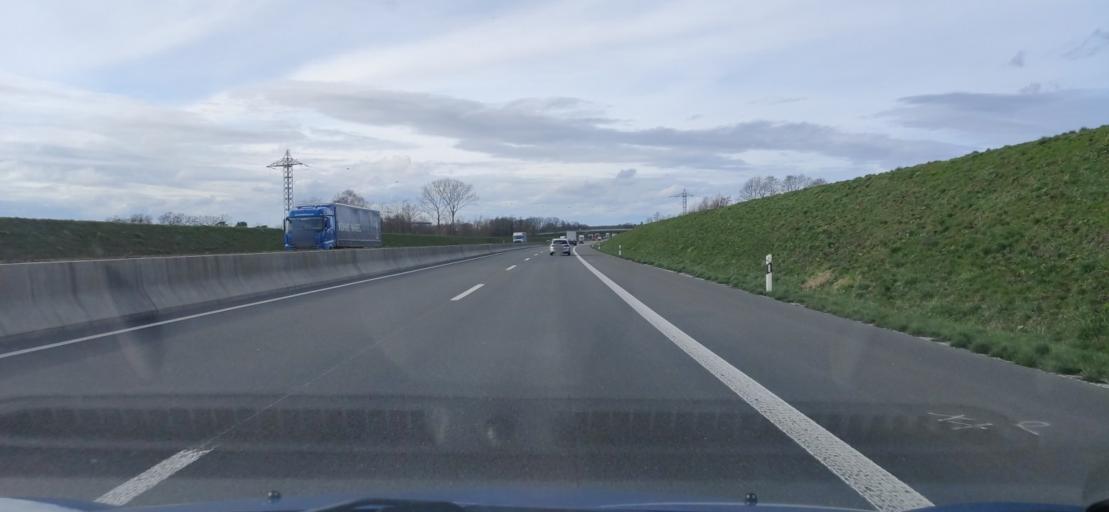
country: DE
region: North Rhine-Westphalia
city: Halle
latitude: 52.0299
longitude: 8.3590
